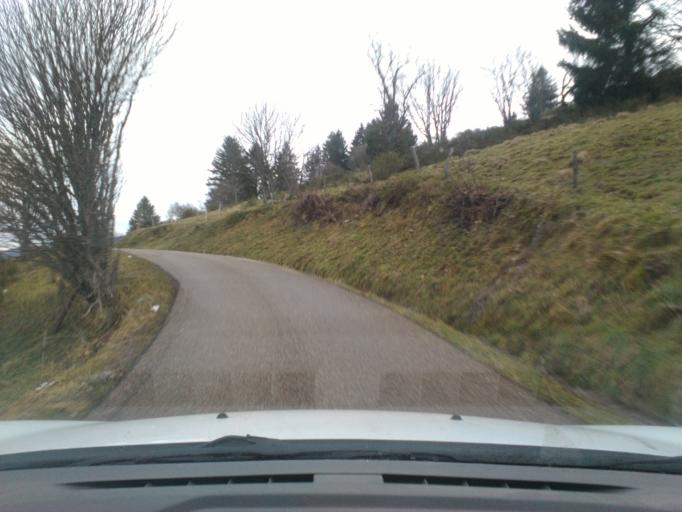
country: FR
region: Lorraine
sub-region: Departement des Vosges
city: La Bresse
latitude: 47.9938
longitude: 6.8767
